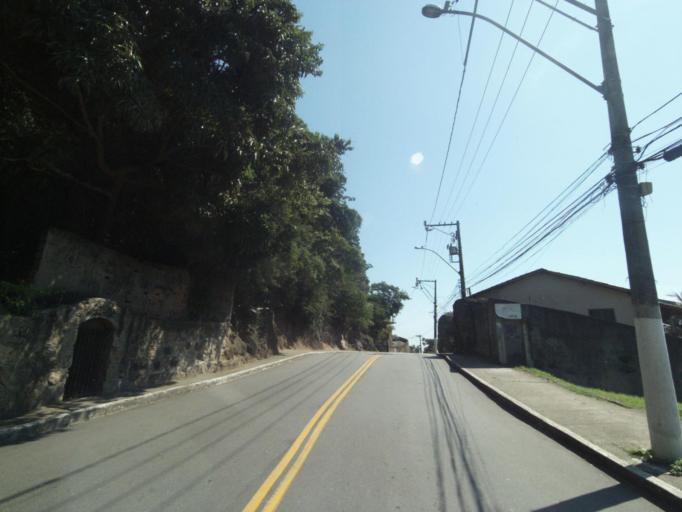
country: BR
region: Rio de Janeiro
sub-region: Niteroi
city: Niteroi
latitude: -22.9290
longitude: -43.1180
